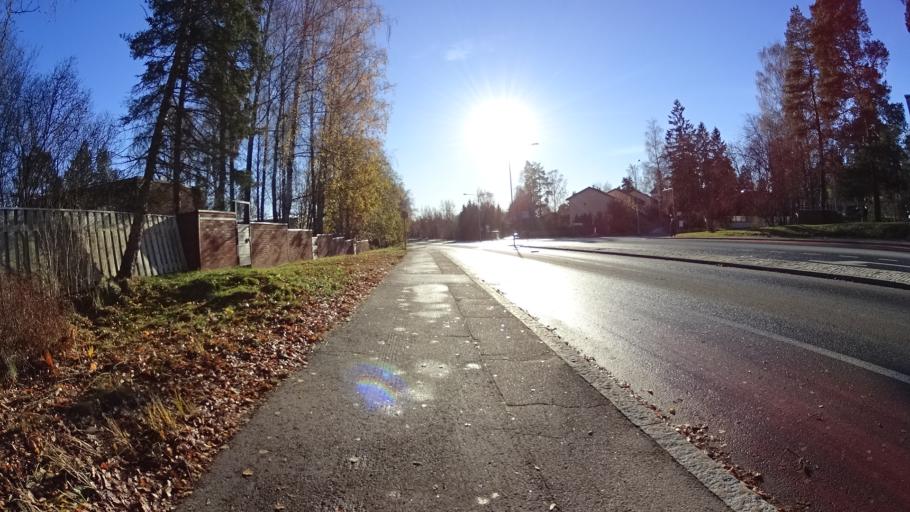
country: FI
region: Uusimaa
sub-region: Helsinki
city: Teekkarikylae
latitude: 60.2334
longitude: 24.8465
